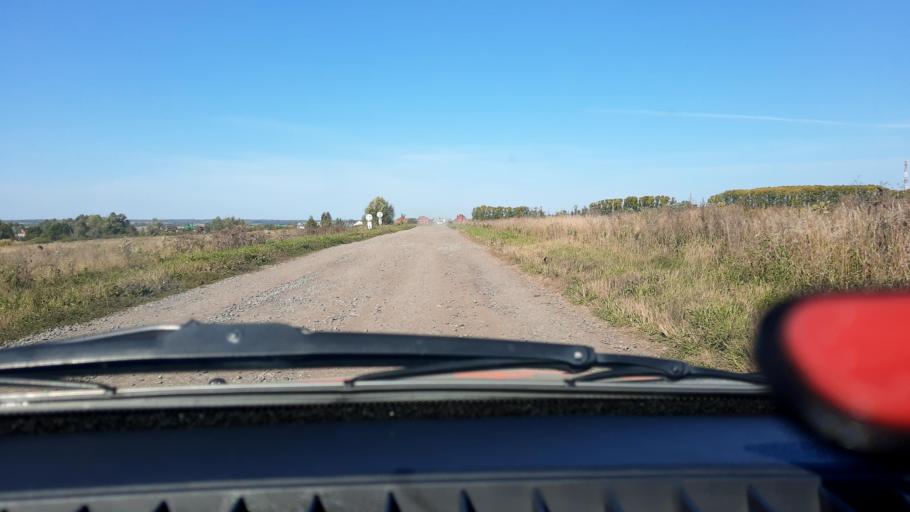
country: RU
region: Bashkortostan
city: Asanovo
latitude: 54.8078
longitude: 55.5853
